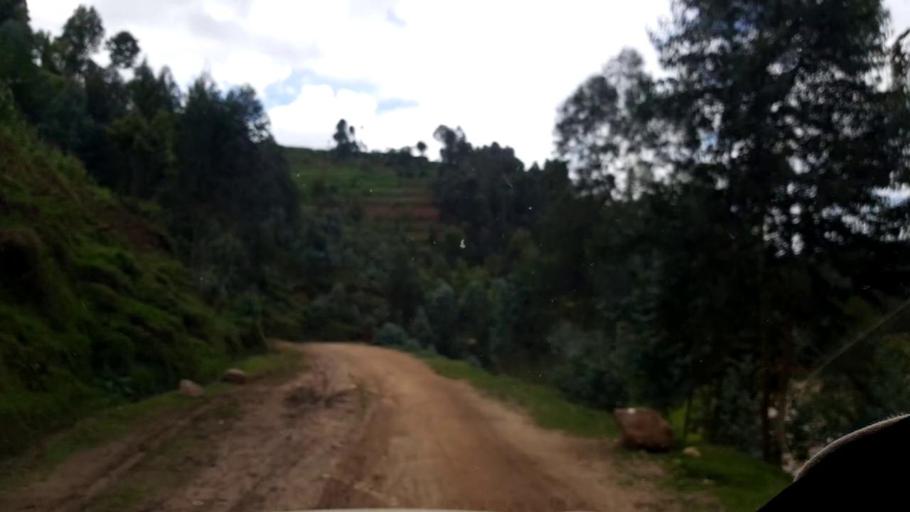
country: RW
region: Western Province
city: Kibuye
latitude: -1.9091
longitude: 29.4570
